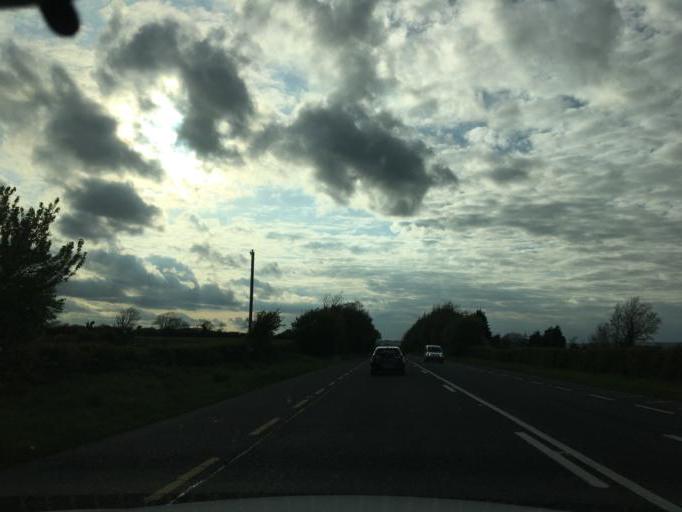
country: IE
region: Leinster
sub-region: Loch Garman
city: Loch Garman
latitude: 52.3439
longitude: -6.5868
